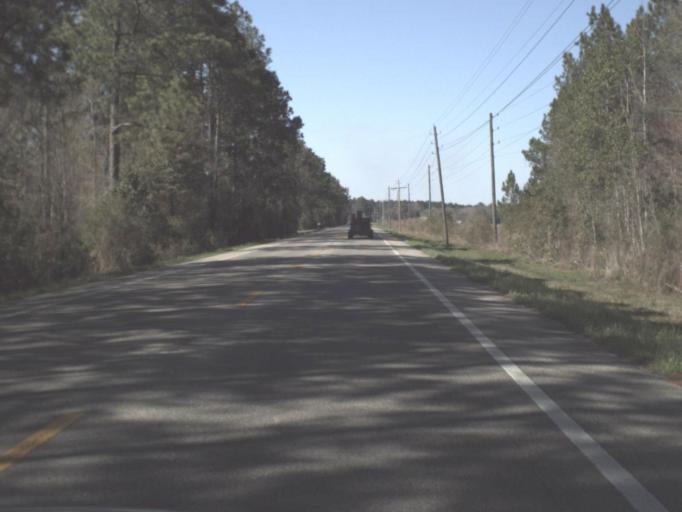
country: US
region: Florida
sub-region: Calhoun County
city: Blountstown
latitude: 30.5224
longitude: -85.1285
